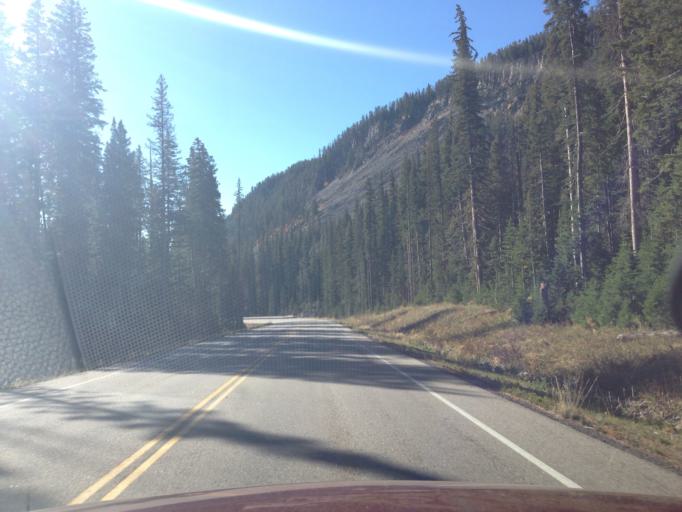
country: US
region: Montana
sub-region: Carbon County
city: Red Lodge
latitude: 45.0128
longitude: -109.8687
